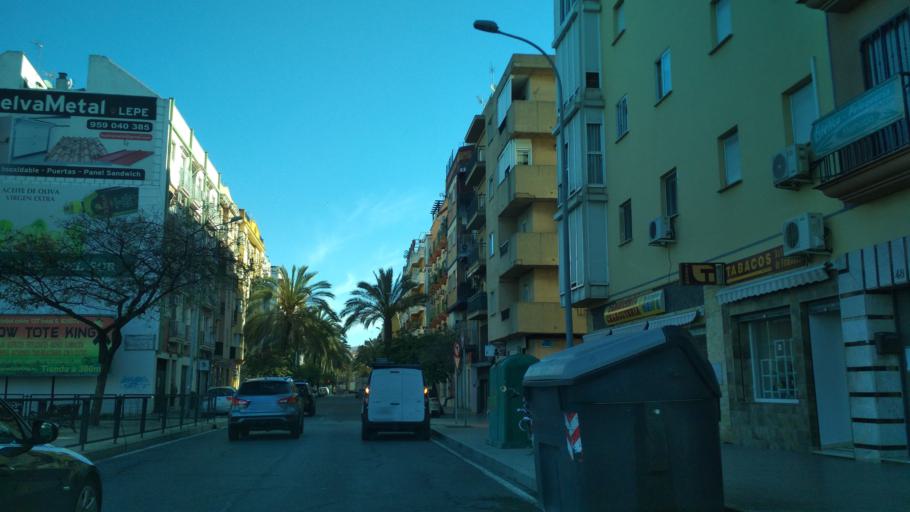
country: ES
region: Andalusia
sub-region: Provincia de Huelva
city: Huelva
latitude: 37.2689
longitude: -6.9514
